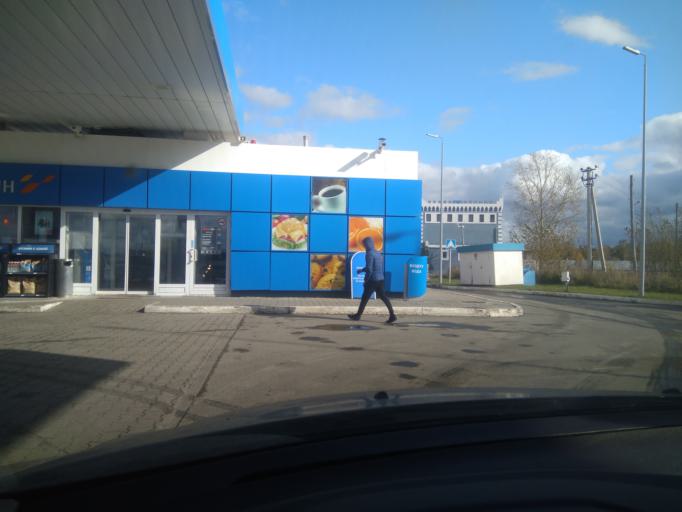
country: RU
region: Sverdlovsk
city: Tugulym
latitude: 57.0734
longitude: 64.5631
